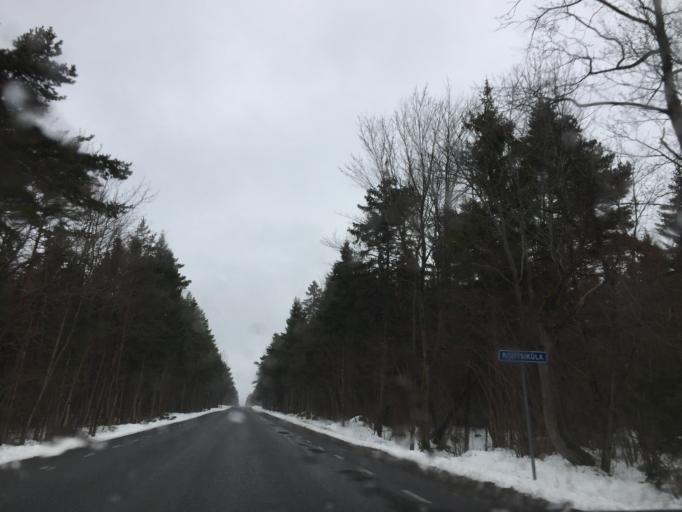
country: EE
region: Saare
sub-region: Kuressaare linn
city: Kuressaare
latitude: 58.3332
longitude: 22.0264
